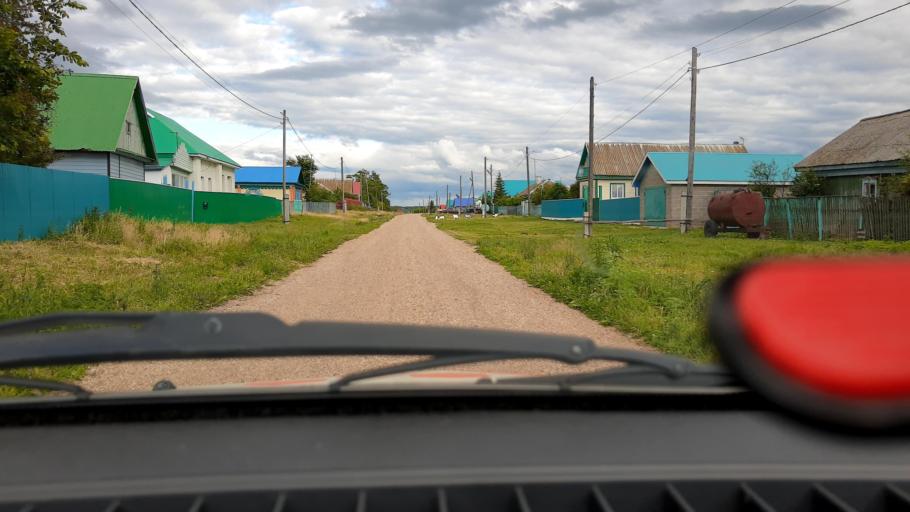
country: RU
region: Bashkortostan
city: Karmaskaly
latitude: 54.4202
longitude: 56.0248
